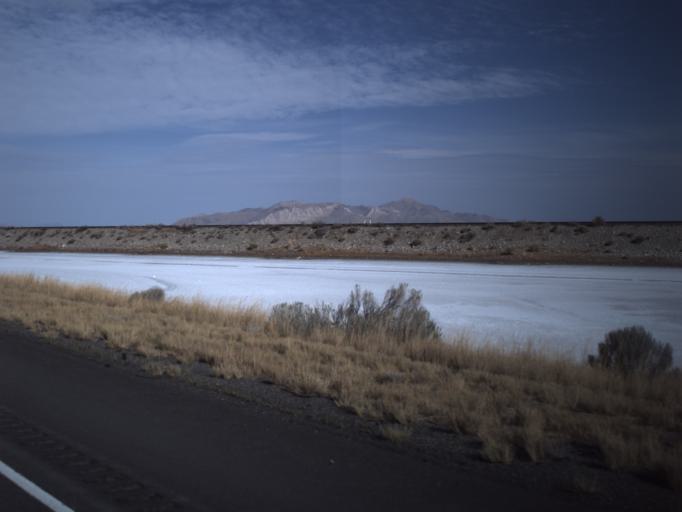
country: US
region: Utah
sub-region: Tooele County
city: Stansbury park
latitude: 40.6668
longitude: -112.3708
